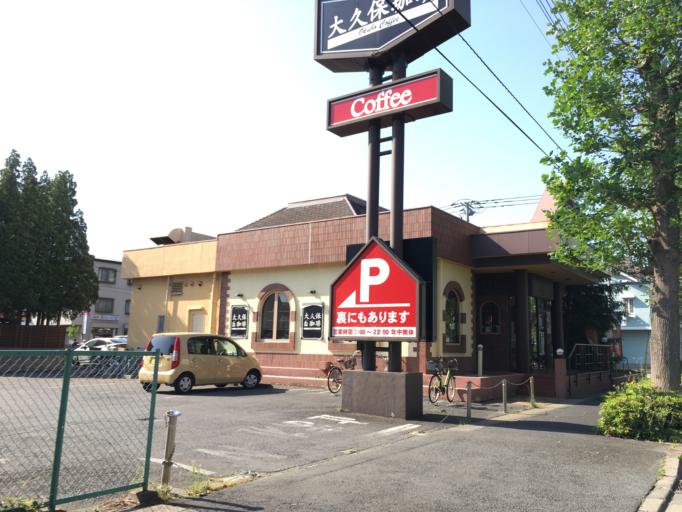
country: JP
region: Chiba
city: Nagareyama
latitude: 35.8208
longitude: 139.9142
